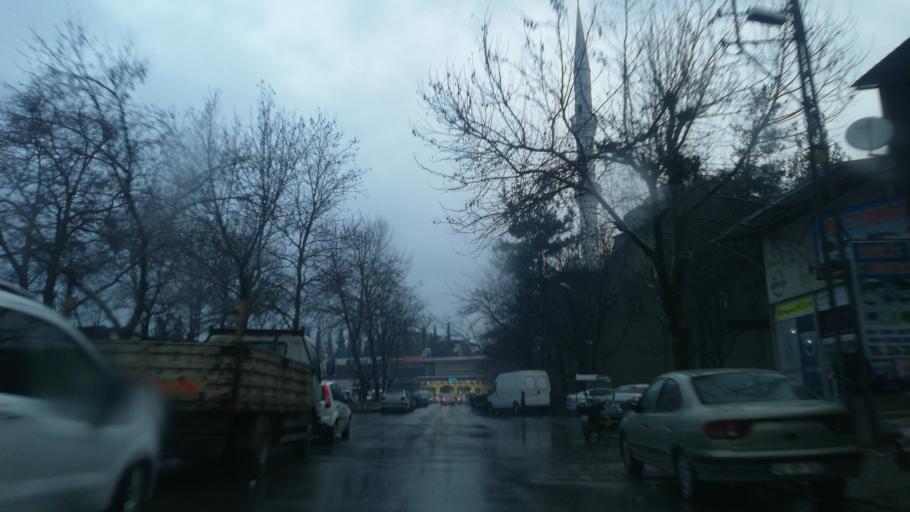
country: TR
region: Kahramanmaras
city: Kahramanmaras
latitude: 37.5646
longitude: 36.9540
